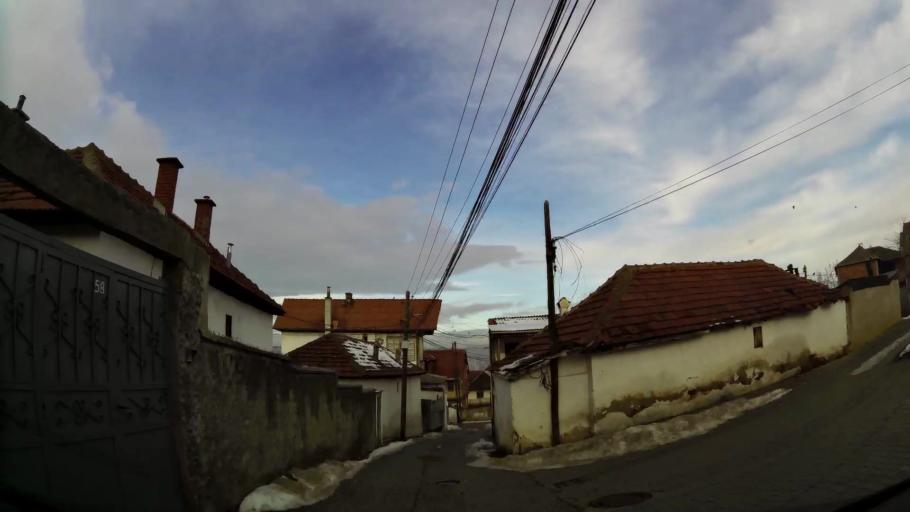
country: XK
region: Pristina
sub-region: Komuna e Prishtines
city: Pristina
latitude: 42.6623
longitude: 21.1727
